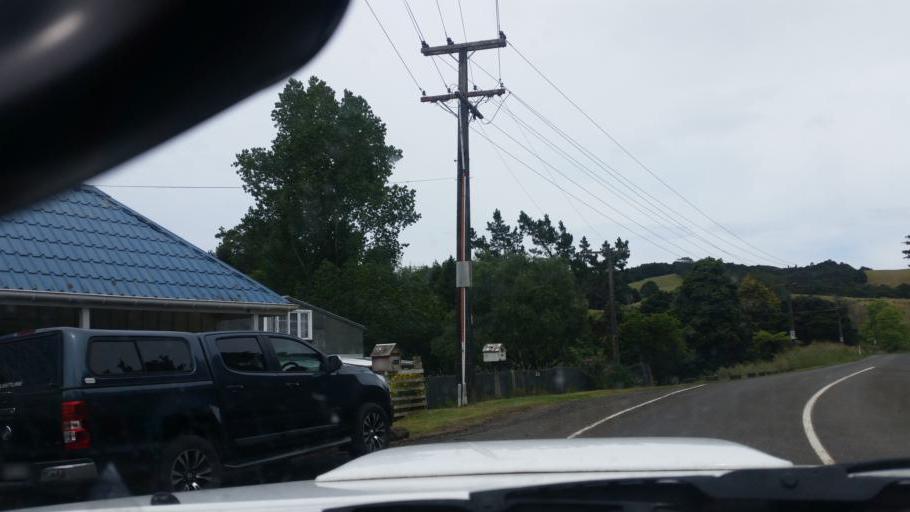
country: NZ
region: Northland
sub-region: Kaipara District
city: Dargaville
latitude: -35.7109
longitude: 173.6179
